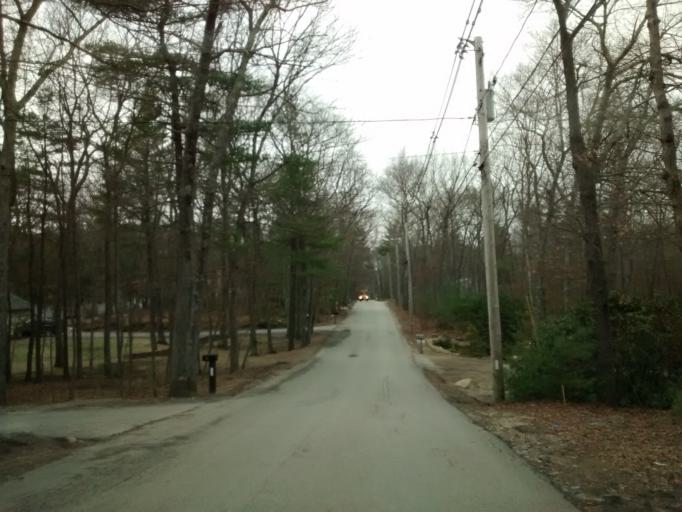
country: US
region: Massachusetts
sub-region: Worcester County
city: Douglas
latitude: 42.0459
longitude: -71.7252
